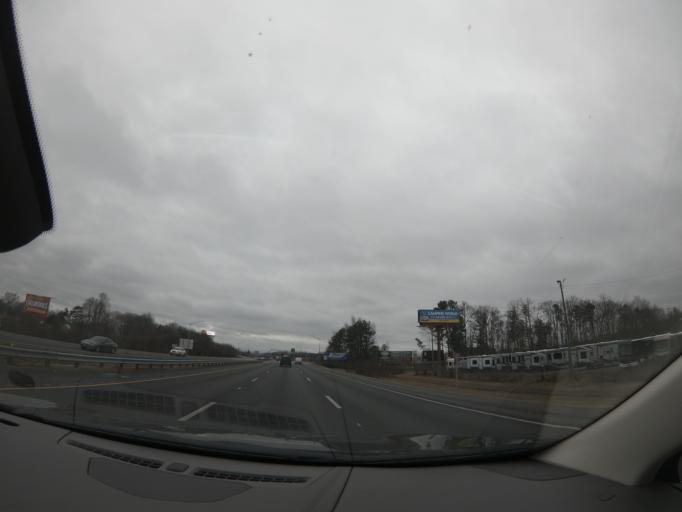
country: US
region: Georgia
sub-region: Catoosa County
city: Indian Springs
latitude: 34.9850
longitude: -85.2008
